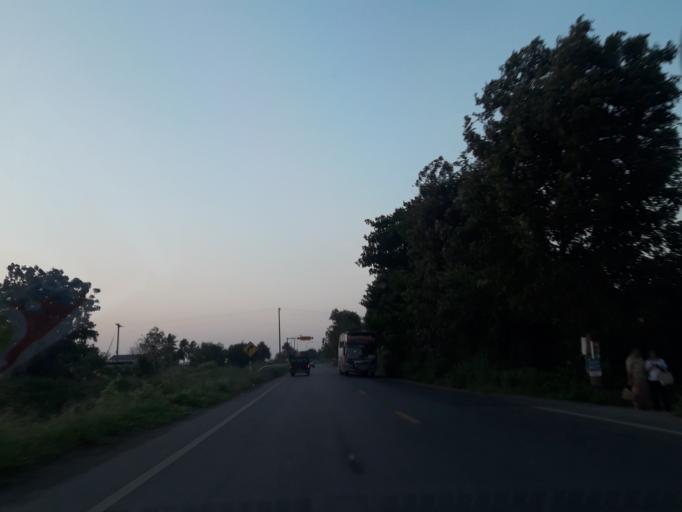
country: TH
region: Phra Nakhon Si Ayutthaya
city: Maha Rat
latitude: 14.5664
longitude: 100.5424
